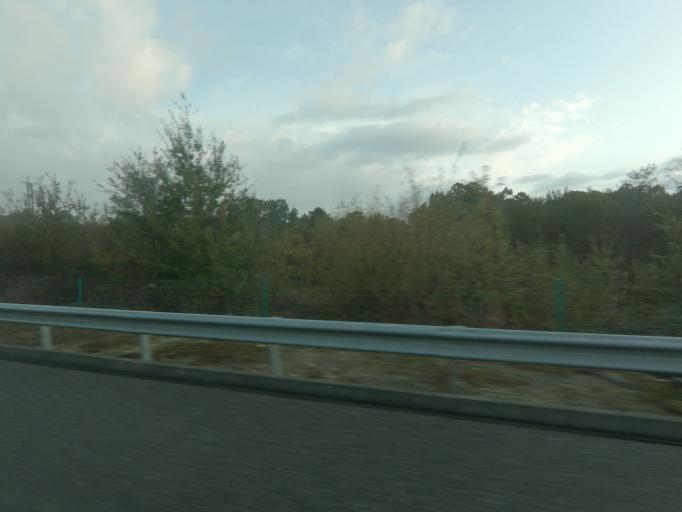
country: ES
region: Galicia
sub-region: Provincia de Pontevedra
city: Tui
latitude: 42.1061
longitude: -8.6486
